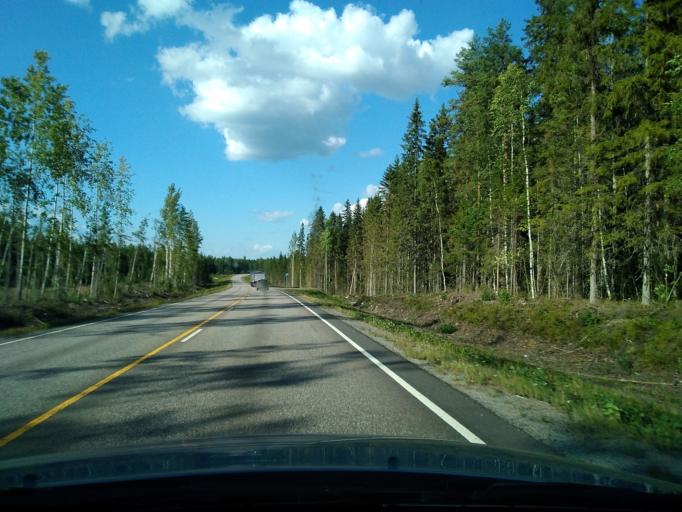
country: FI
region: Central Finland
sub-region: Keuruu
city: Keuruu
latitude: 62.1525
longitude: 24.7503
